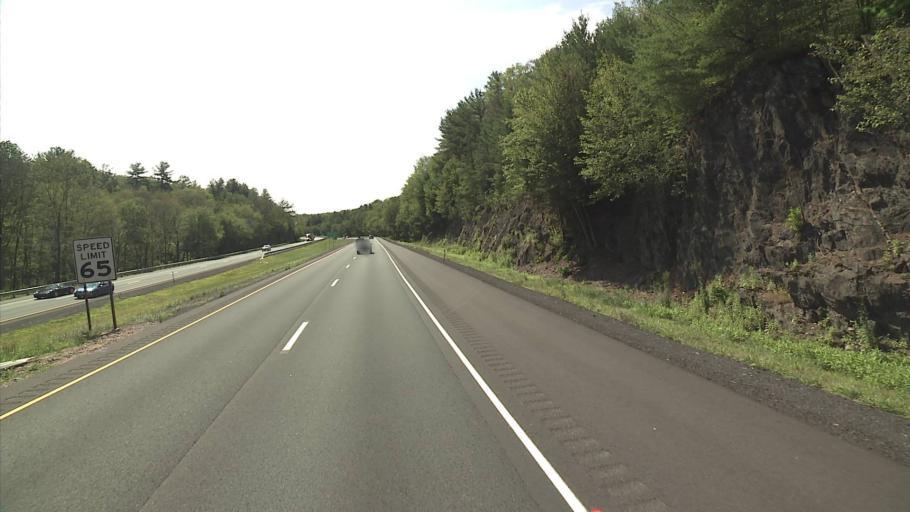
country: US
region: Connecticut
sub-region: Hartford County
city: Terramuggus
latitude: 41.6554
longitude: -72.5030
